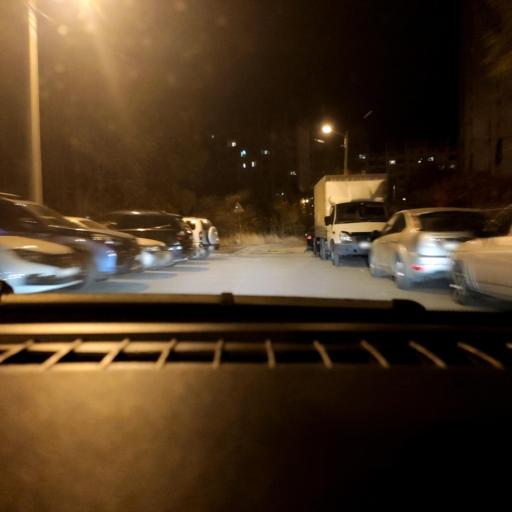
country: RU
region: Voronezj
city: Podgornoye
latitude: 51.7208
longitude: 39.1698
